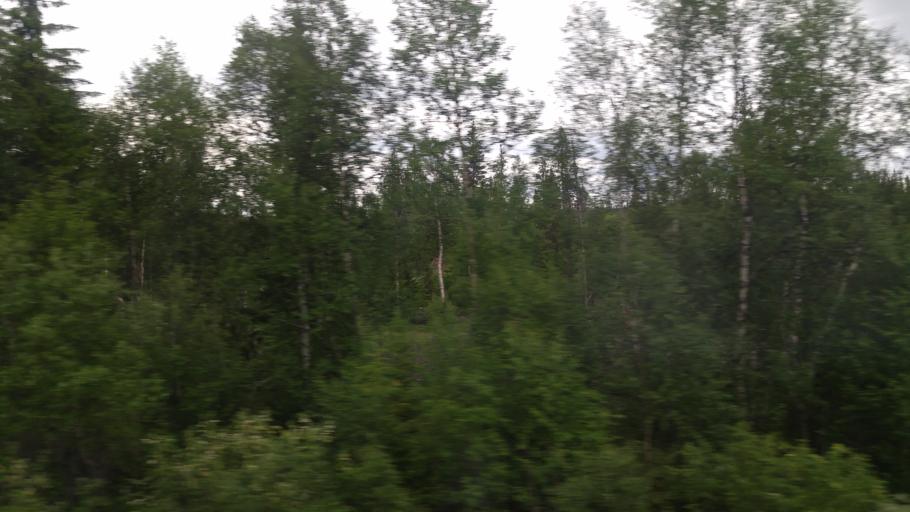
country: NO
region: Nord-Trondelag
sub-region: Meraker
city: Meraker
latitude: 63.2875
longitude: 12.3521
